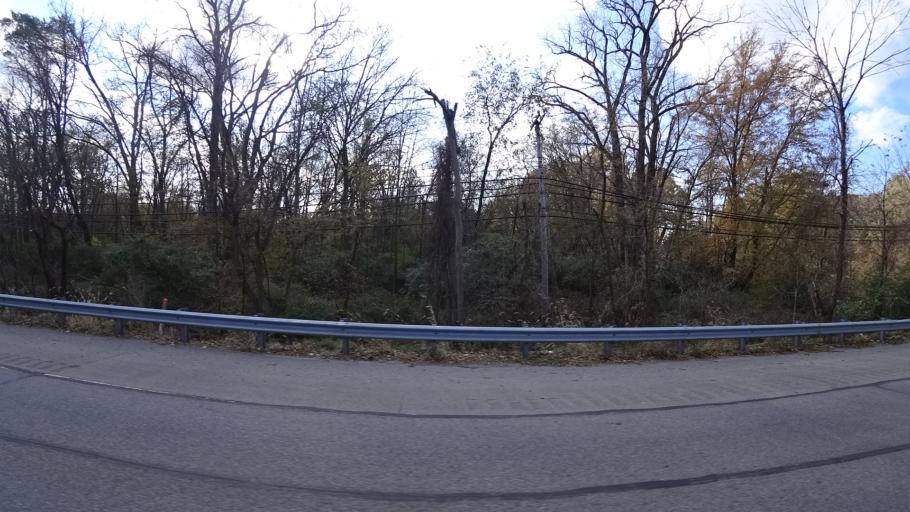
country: US
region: Indiana
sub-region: LaPorte County
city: Trail Creek
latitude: 41.7052
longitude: -86.8559
